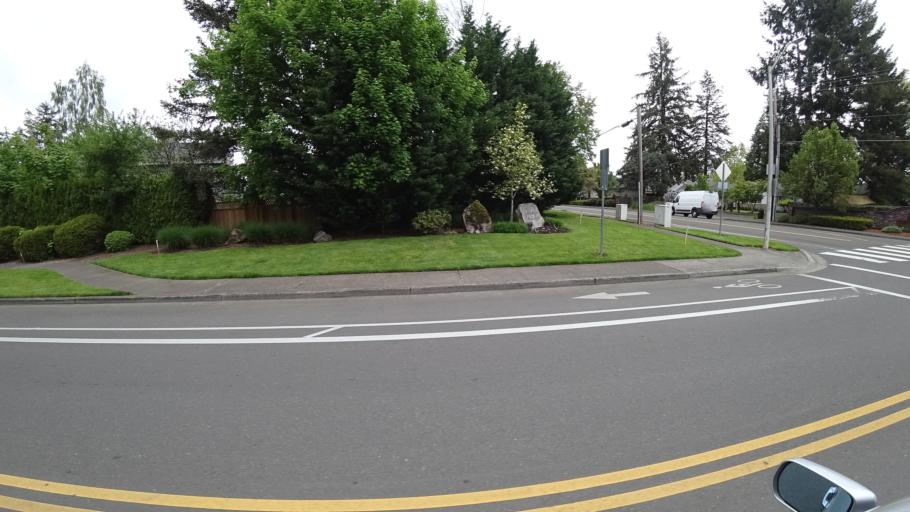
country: US
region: Oregon
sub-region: Washington County
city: Hillsboro
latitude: 45.5390
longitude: -122.9800
